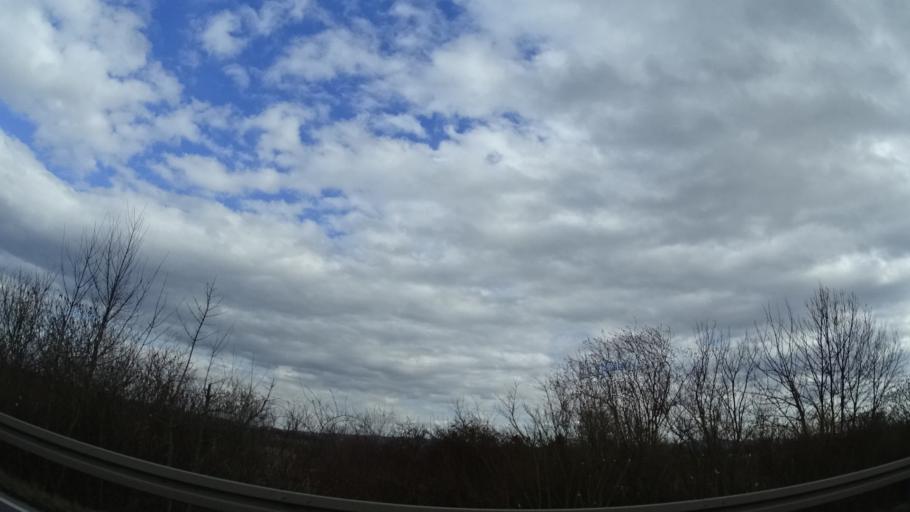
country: DE
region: Hesse
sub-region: Regierungsbezirk Darmstadt
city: Stockstadt am Rhein
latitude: 49.7972
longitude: 8.4843
